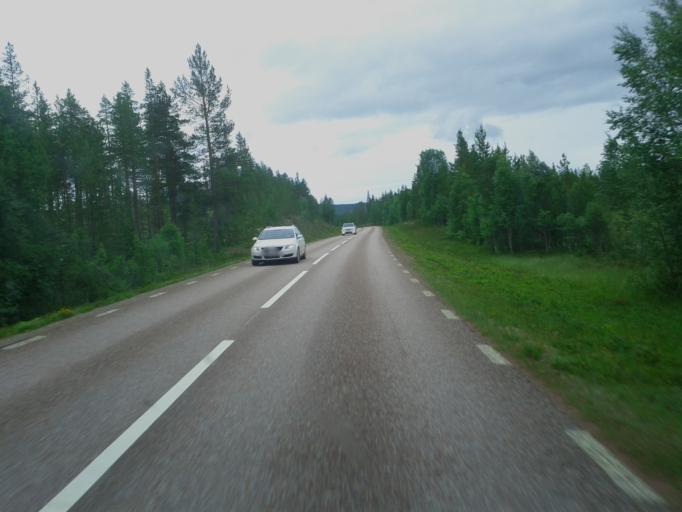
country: NO
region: Hedmark
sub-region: Trysil
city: Innbygda
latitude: 61.7031
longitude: 13.0254
